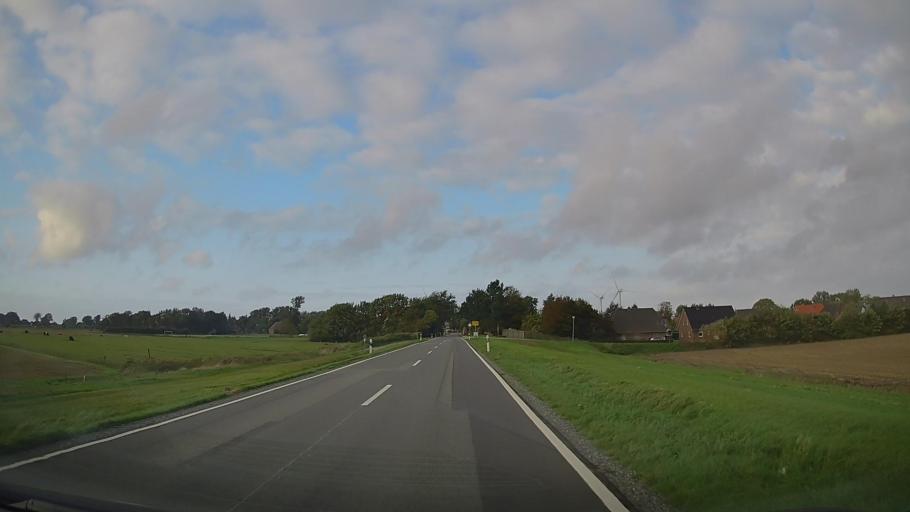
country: DE
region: Schleswig-Holstein
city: Simonsberg
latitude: 54.4309
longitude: 8.9751
